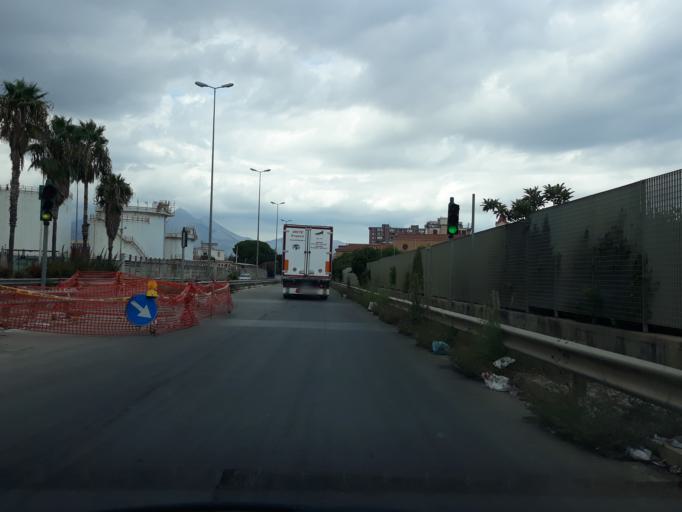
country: IT
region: Sicily
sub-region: Palermo
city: Ciaculli
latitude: 38.0927
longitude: 13.4069
